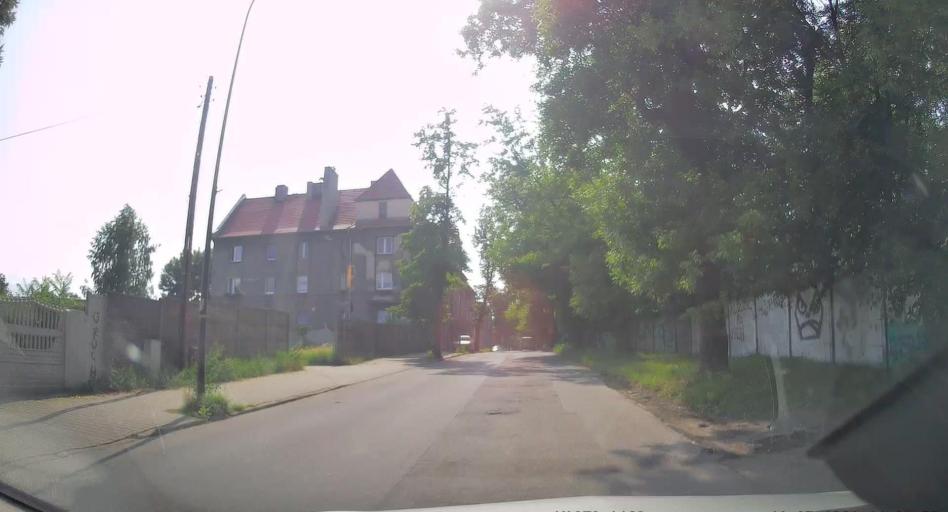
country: PL
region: Silesian Voivodeship
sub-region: Bytom
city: Bytom
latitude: 50.3294
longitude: 18.9364
